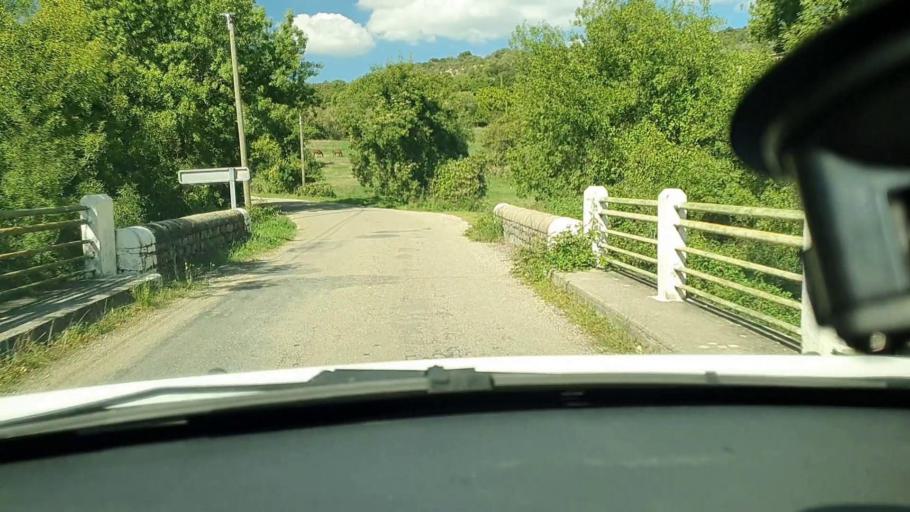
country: FR
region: Languedoc-Roussillon
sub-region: Departement du Gard
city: Goudargues
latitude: 44.1727
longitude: 4.3844
